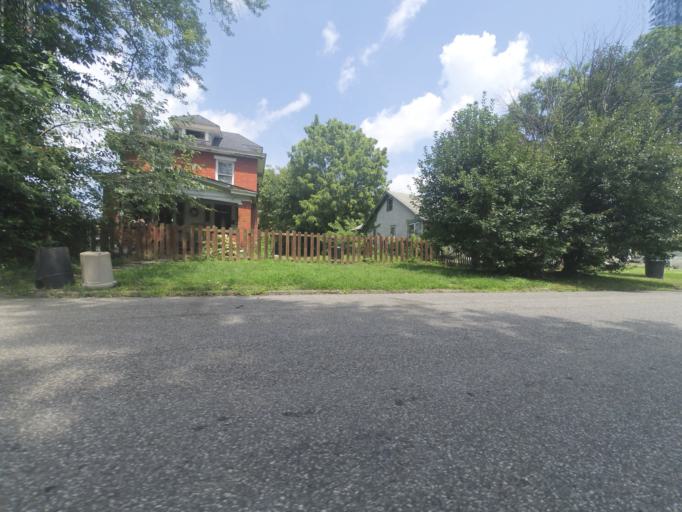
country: US
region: West Virginia
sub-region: Cabell County
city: Huntington
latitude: 38.4149
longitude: -82.4190
